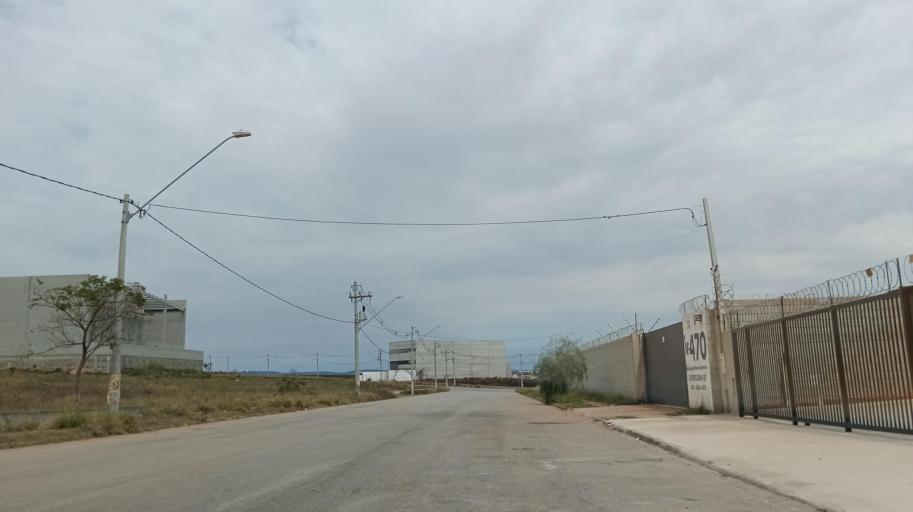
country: BR
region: Sao Paulo
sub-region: Sorocaba
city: Sorocaba
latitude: -23.4560
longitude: -47.4562
